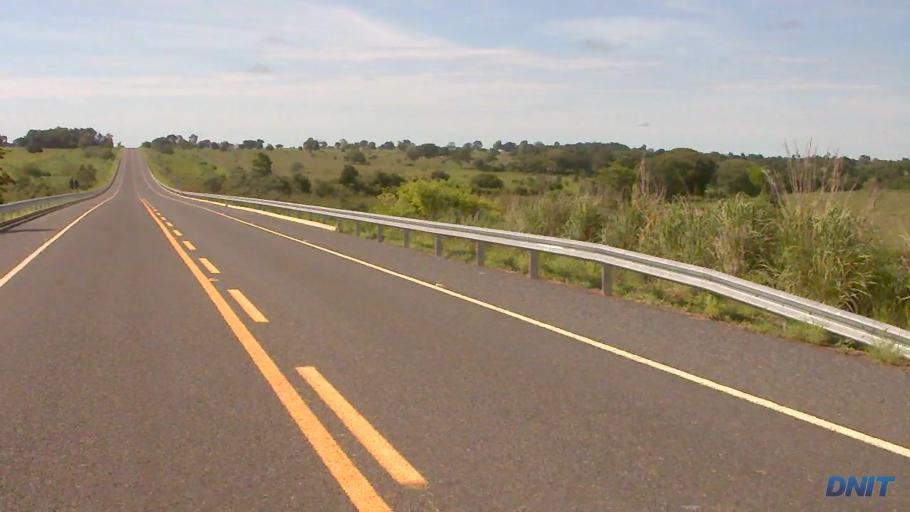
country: BR
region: Goias
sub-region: Sao Miguel Do Araguaia
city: Sao Miguel do Araguaia
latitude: -13.4487
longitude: -50.1212
